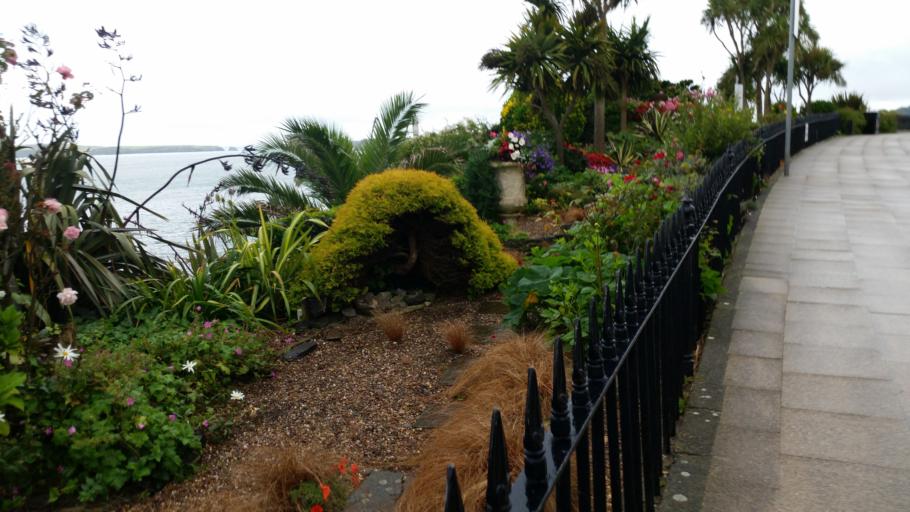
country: GB
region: Wales
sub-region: Pembrokeshire
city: Tenby
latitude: 51.6690
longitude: -4.7003
